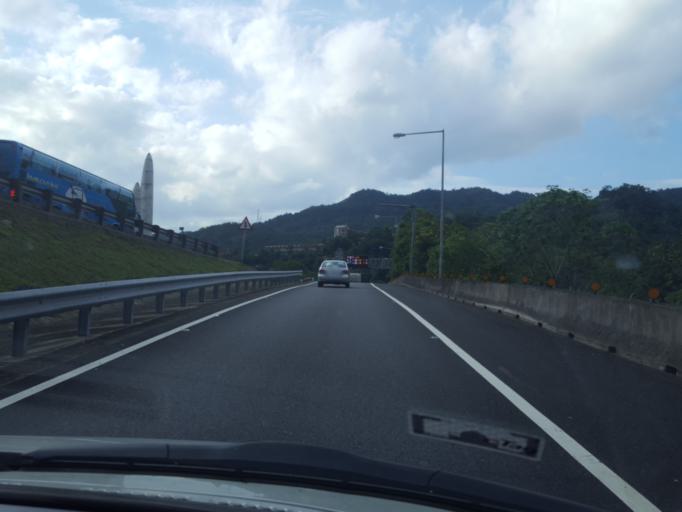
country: TW
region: Taipei
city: Taipei
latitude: 25.0095
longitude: 121.6471
